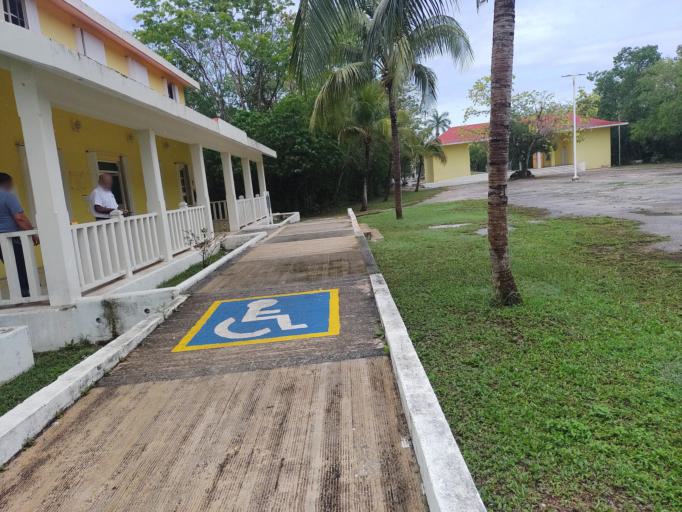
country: MX
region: Quintana Roo
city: San Miguel de Cozumel
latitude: 20.4893
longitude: -86.9409
